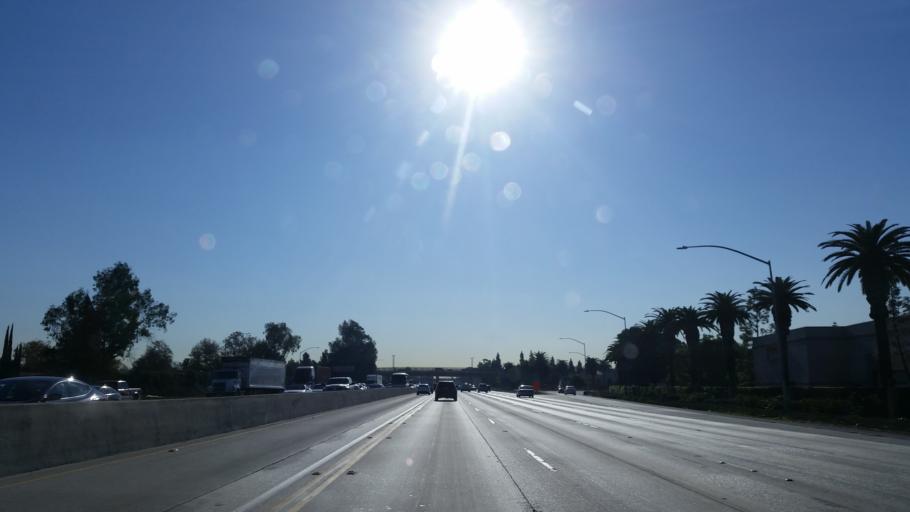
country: US
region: California
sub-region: Los Angeles County
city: Cerritos
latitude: 33.8724
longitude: -118.0592
